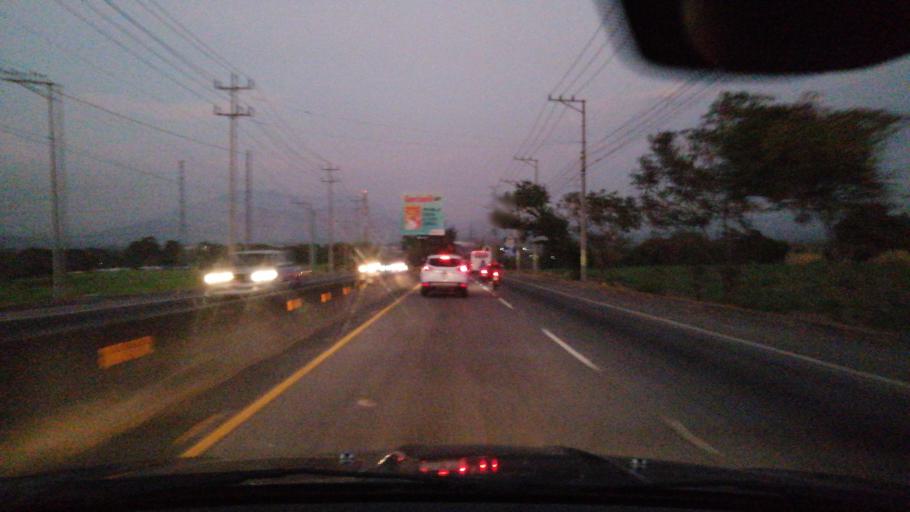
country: SV
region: San Salvador
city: Ayutuxtepeque
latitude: 13.7720
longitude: -89.2107
